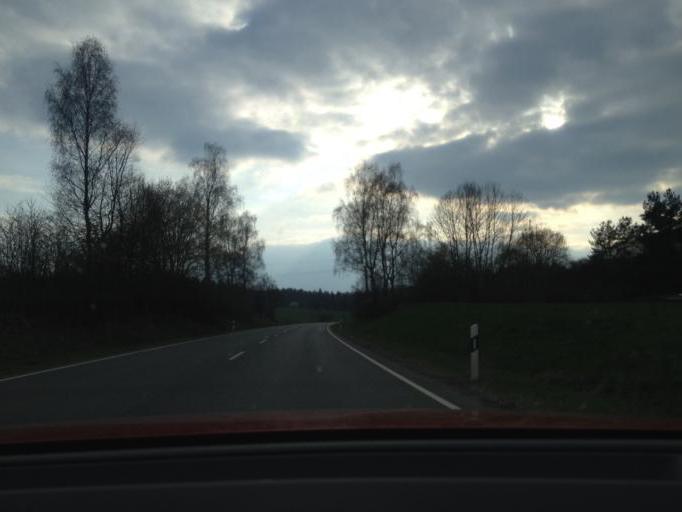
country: DE
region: Bavaria
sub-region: Upper Palatinate
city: Kirchenthumbach
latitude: 49.7387
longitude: 11.7204
